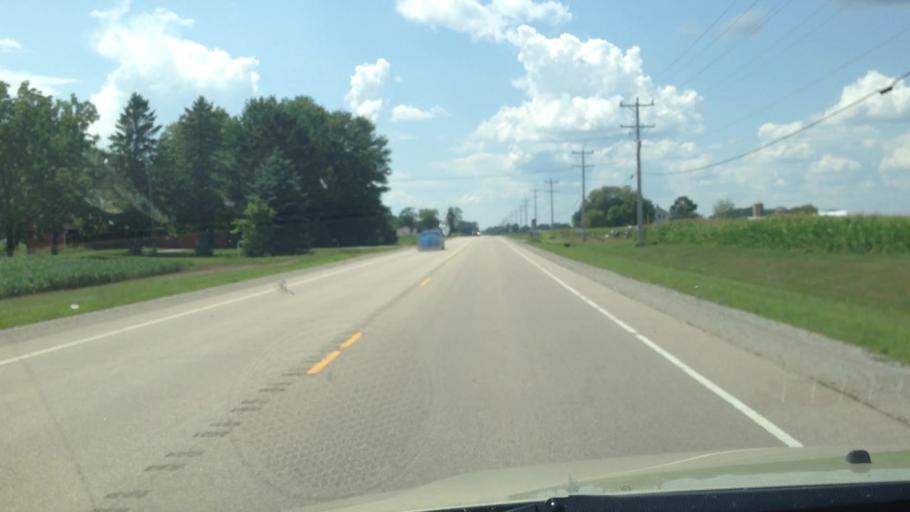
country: US
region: Wisconsin
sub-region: Brown County
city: Pulaski
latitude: 44.6730
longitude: -88.2642
